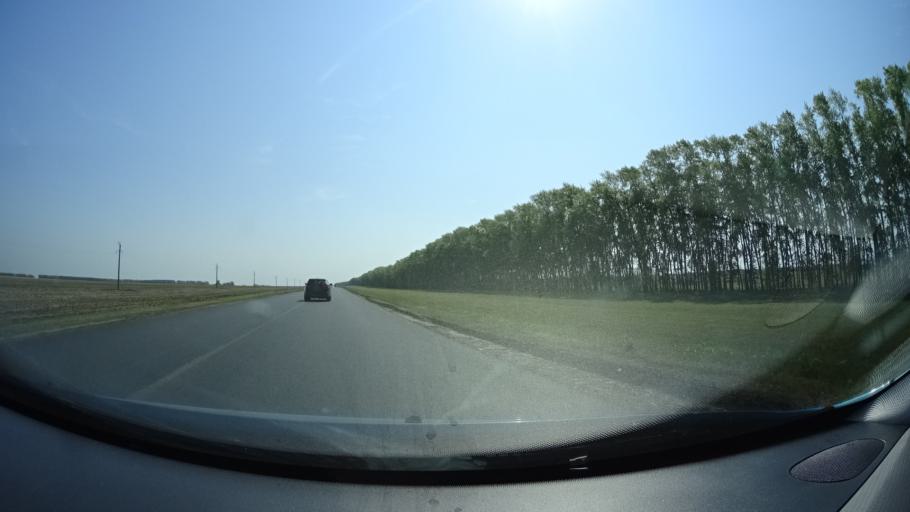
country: RU
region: Bashkortostan
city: Karmaskaly
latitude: 54.4149
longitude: 56.0571
